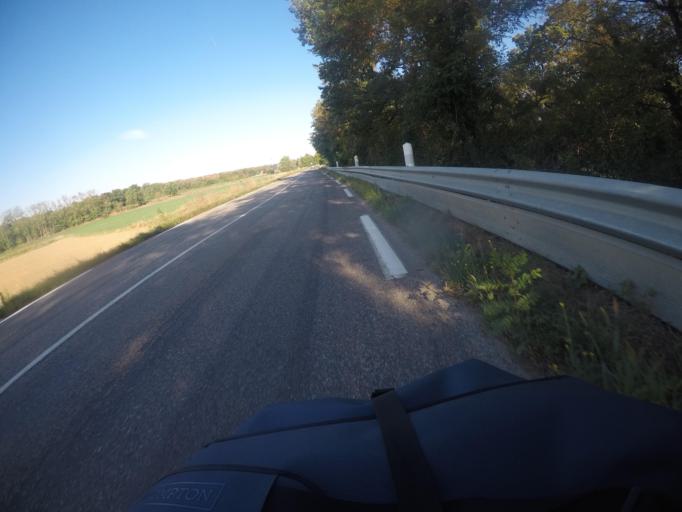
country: FR
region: Alsace
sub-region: Departement du Haut-Rhin
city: Rosenau
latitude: 47.6333
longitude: 7.5224
